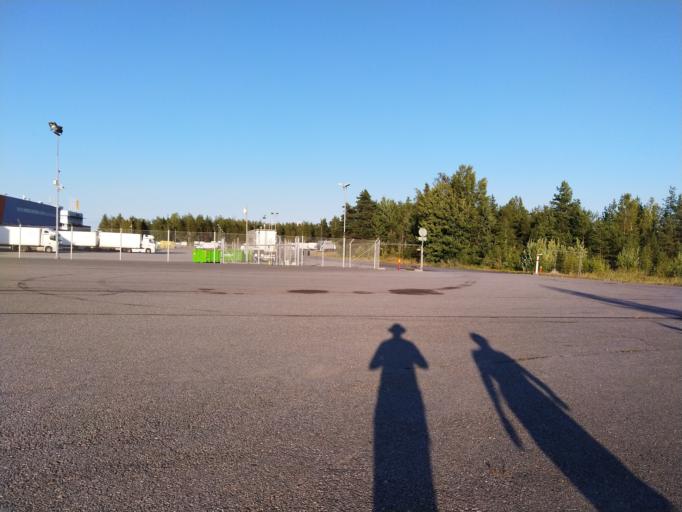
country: FI
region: Varsinais-Suomi
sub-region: Turku
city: Rusko
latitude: 60.5096
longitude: 22.2610
